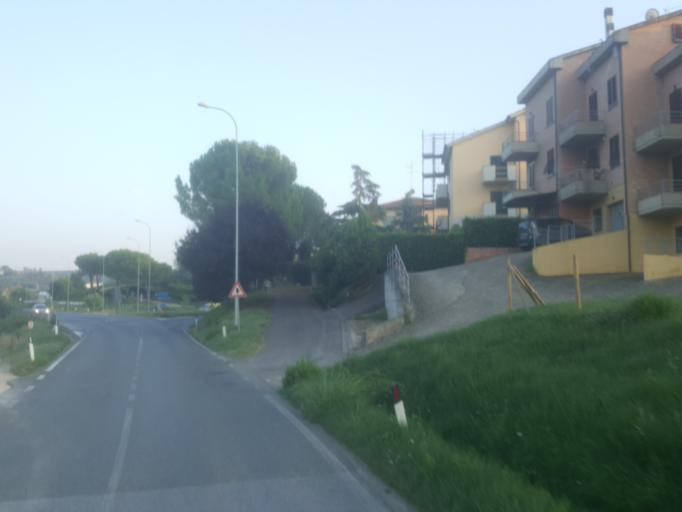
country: IT
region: Tuscany
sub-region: Province of Florence
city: Certaldo
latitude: 43.5405
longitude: 11.0329
